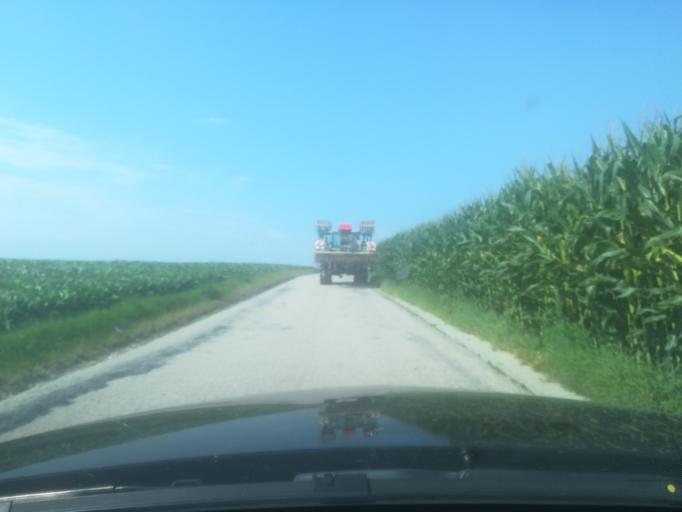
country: AT
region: Upper Austria
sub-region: Wels-Land
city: Holzhausen
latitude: 48.2173
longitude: 14.0693
